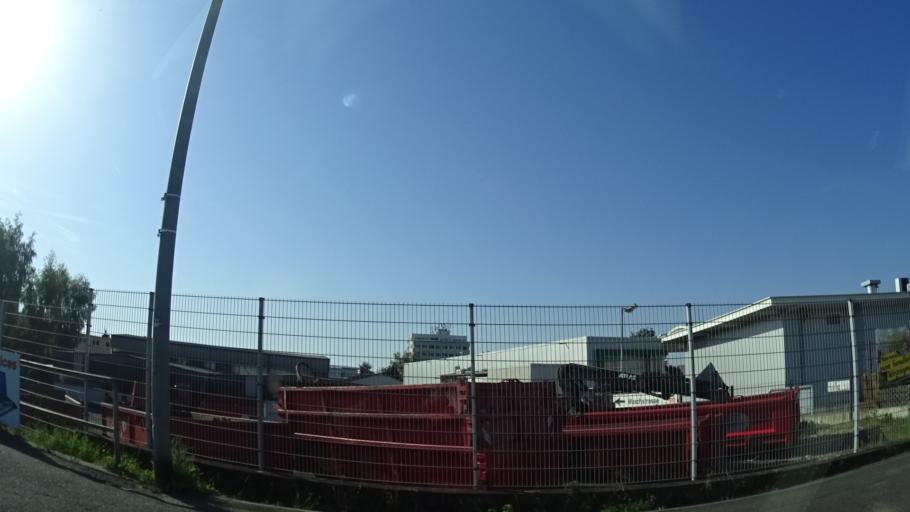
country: DE
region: Hesse
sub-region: Regierungsbezirk Darmstadt
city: Steinbach am Taunus
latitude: 50.1716
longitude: 8.5830
